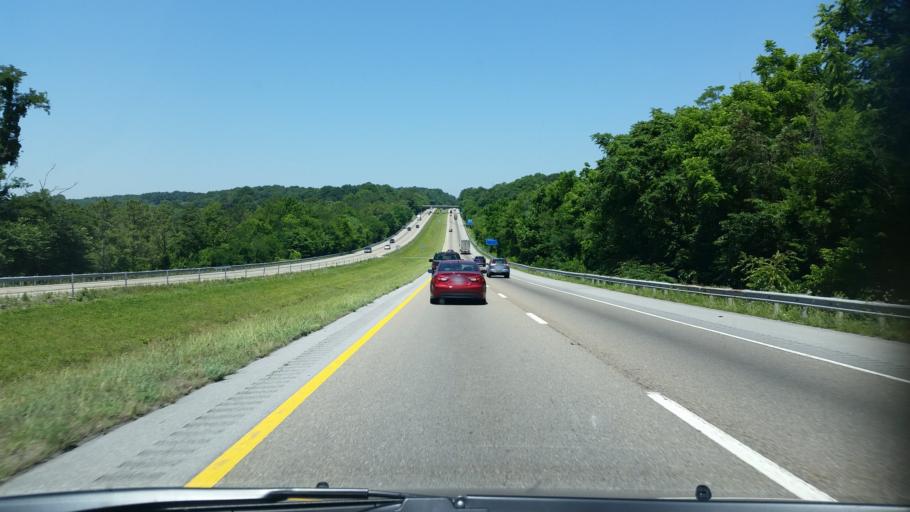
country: US
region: Tennessee
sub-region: Roane County
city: Kingston
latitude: 35.8642
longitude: -84.4183
